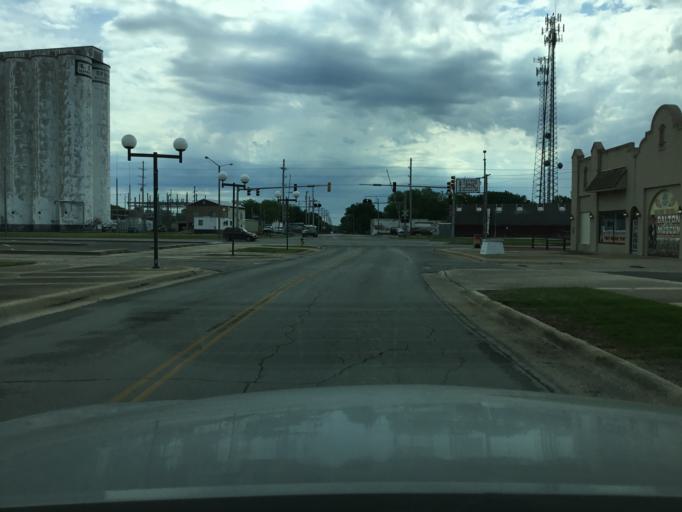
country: US
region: Kansas
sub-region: Montgomery County
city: Coffeyville
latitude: 37.0361
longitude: -95.6149
